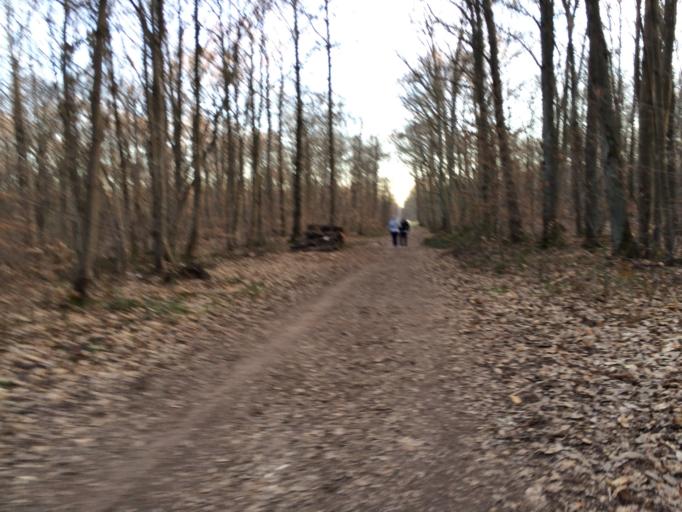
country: FR
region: Ile-de-France
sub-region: Departement des Hauts-de-Seine
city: Meudon
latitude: 48.8022
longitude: 2.2485
